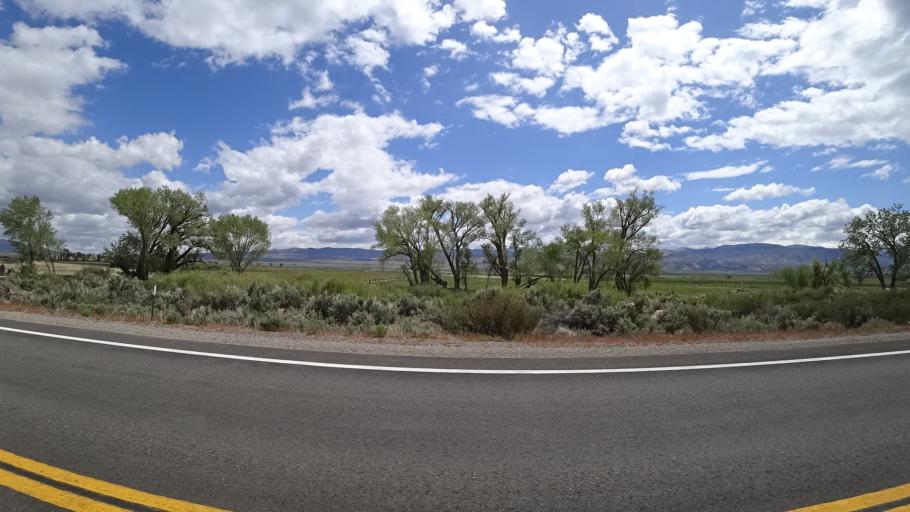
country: US
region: Nevada
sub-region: Lyon County
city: Smith Valley
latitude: 38.6330
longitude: -119.5234
